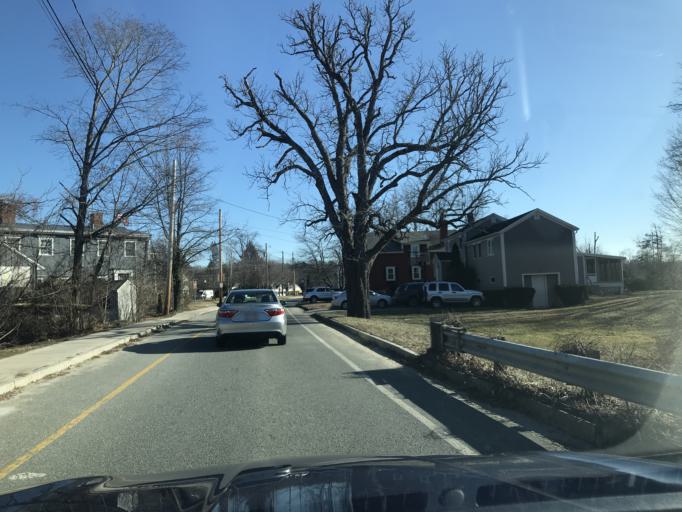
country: US
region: Massachusetts
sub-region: Essex County
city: Groveland
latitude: 42.7228
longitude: -70.9908
